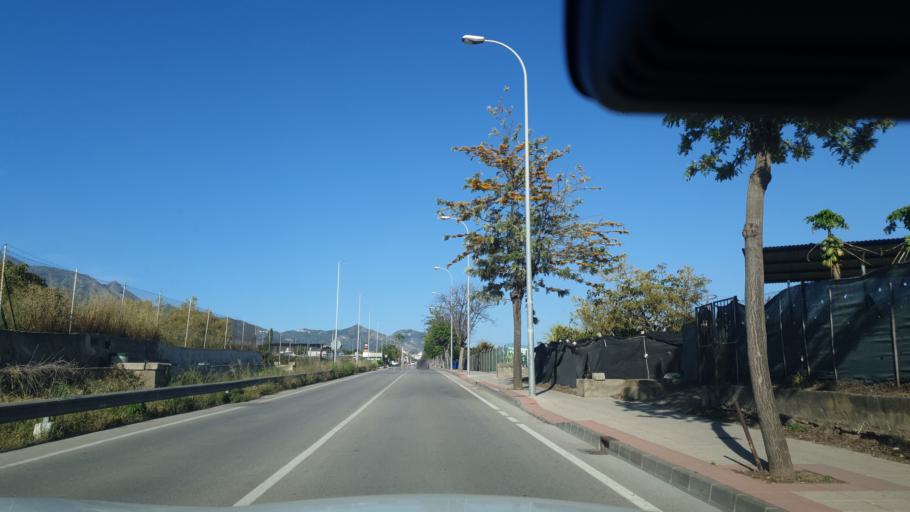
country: ES
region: Andalusia
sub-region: Provincia de Malaga
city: Nerja
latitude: 36.7462
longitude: -3.8939
